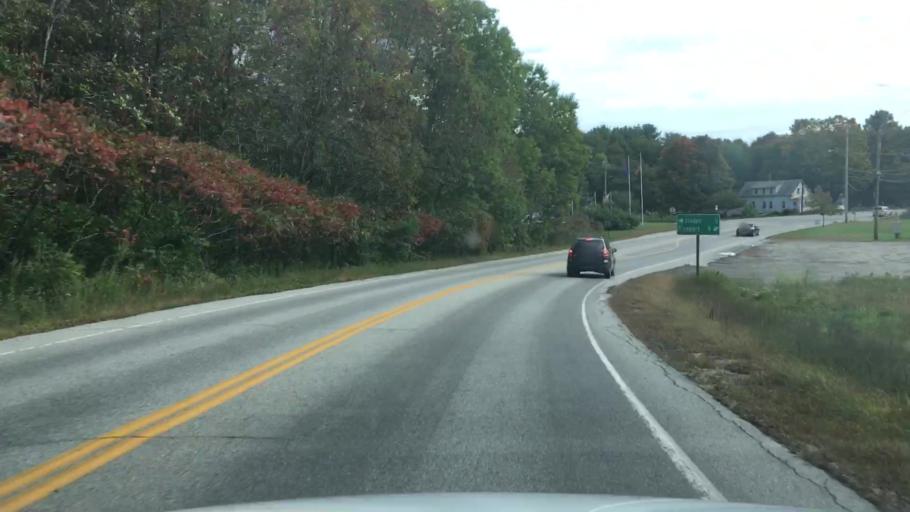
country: US
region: Maine
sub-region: Androscoggin County
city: Lisbon
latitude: 43.9813
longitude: -70.1267
